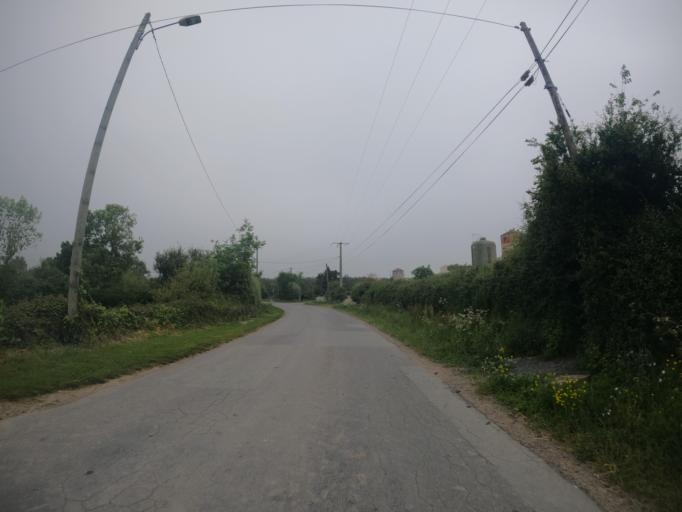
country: FR
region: Poitou-Charentes
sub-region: Departement des Deux-Sevres
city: Mauze-Thouarsais
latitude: 46.8986
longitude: -0.3395
